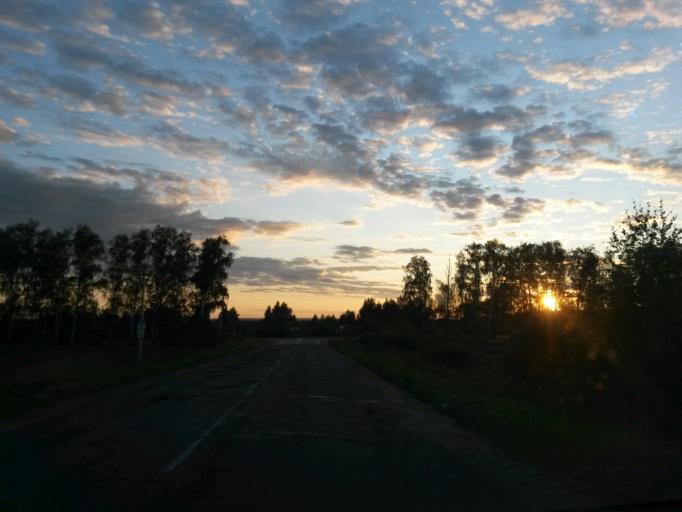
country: RU
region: Jaroslavl
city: Gavrilov-Yam
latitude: 57.3598
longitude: 39.9107
